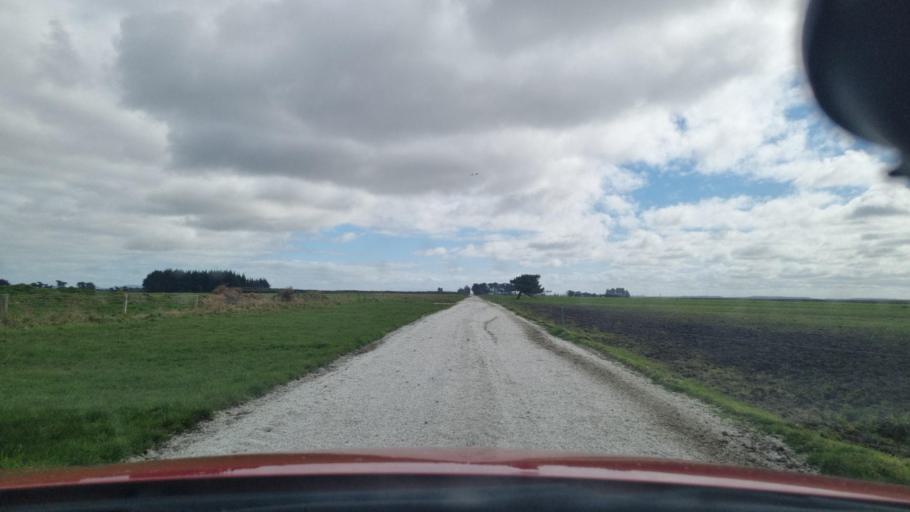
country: NZ
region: Southland
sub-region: Invercargill City
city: Bluff
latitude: -46.5640
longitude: 168.4975
